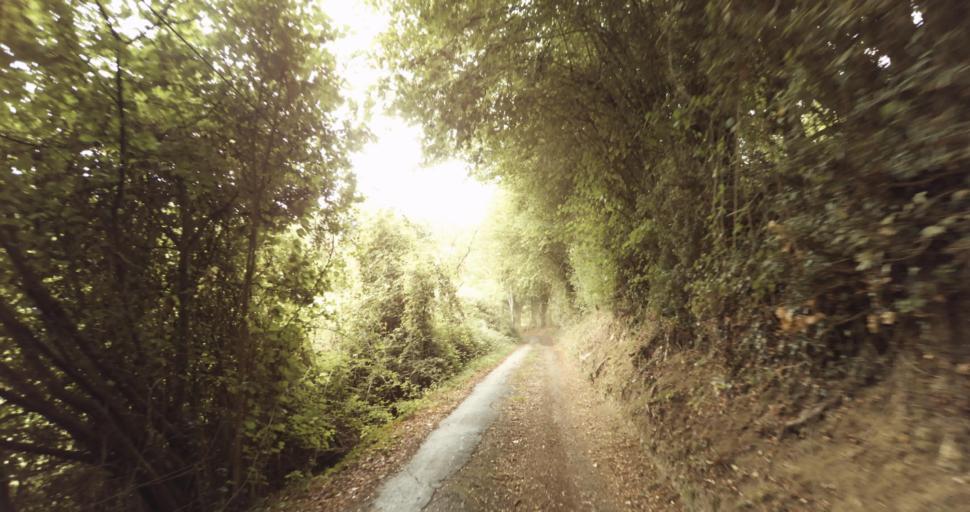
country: FR
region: Lower Normandy
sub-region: Departement de l'Orne
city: Vimoutiers
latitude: 48.8619
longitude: 0.1742
